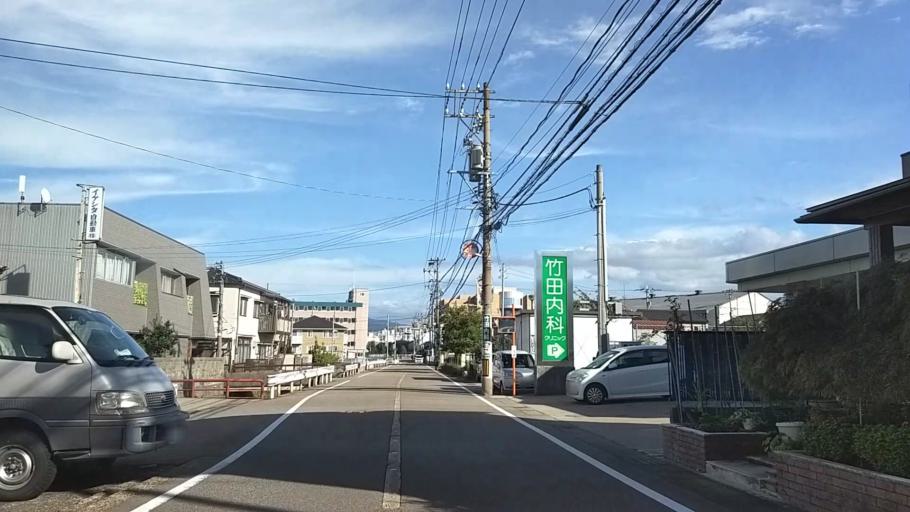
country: JP
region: Ishikawa
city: Kanazawa-shi
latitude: 36.5754
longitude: 136.6394
